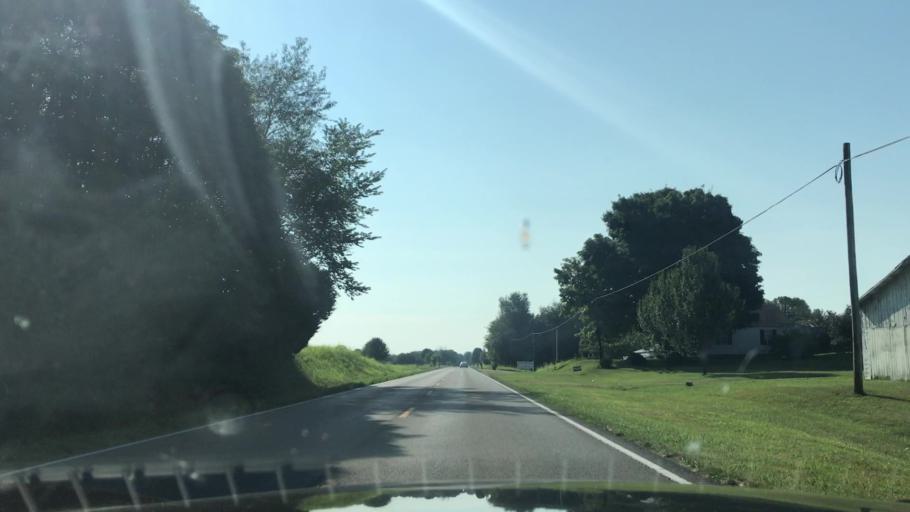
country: US
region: Kentucky
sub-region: Hart County
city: Horse Cave
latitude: 37.1709
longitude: -85.8549
